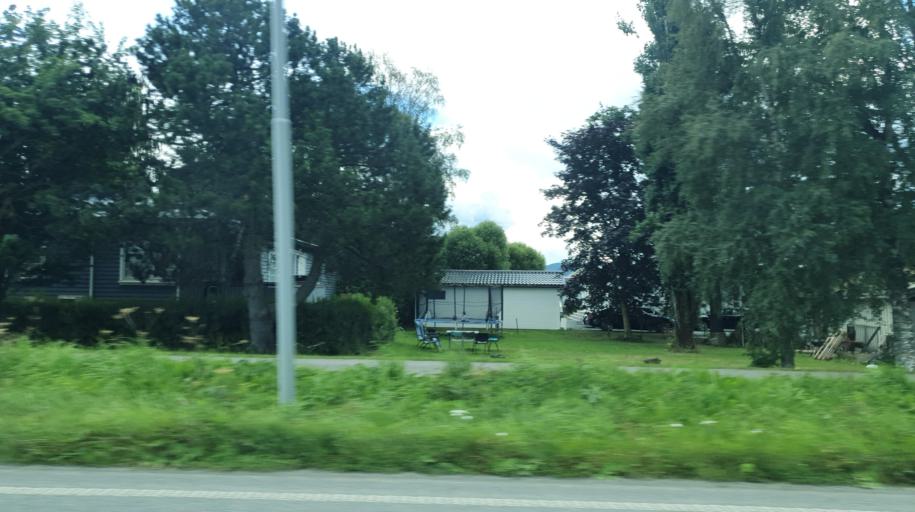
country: NO
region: Nord-Trondelag
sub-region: Levanger
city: Levanger
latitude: 63.7518
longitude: 11.3392
